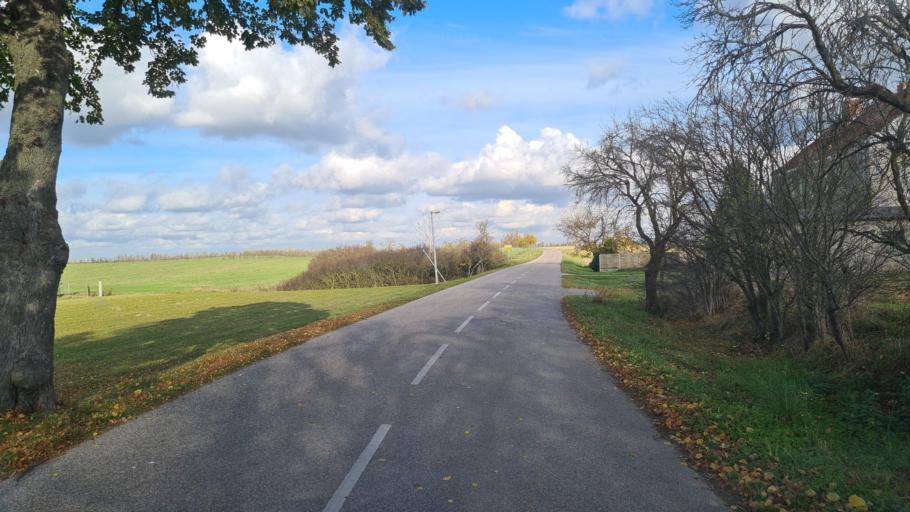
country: DE
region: Saxony-Anhalt
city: Kropstadt
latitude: 52.0098
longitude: 12.7234
